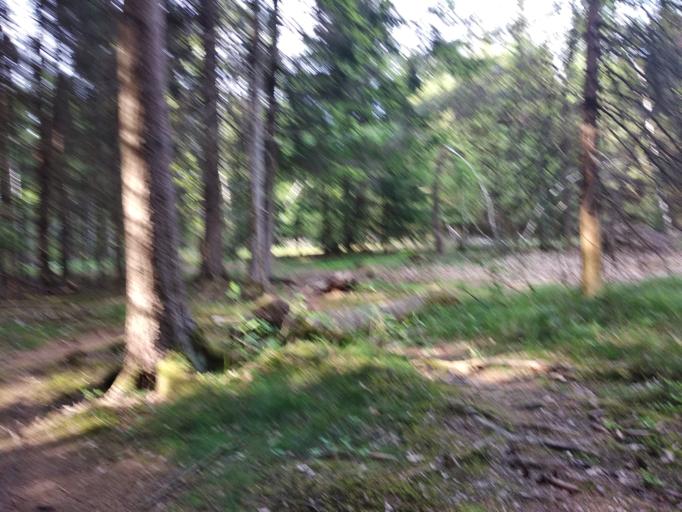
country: DE
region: Bavaria
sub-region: Upper Bavaria
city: Vaterstetten
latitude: 48.1170
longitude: 11.7600
